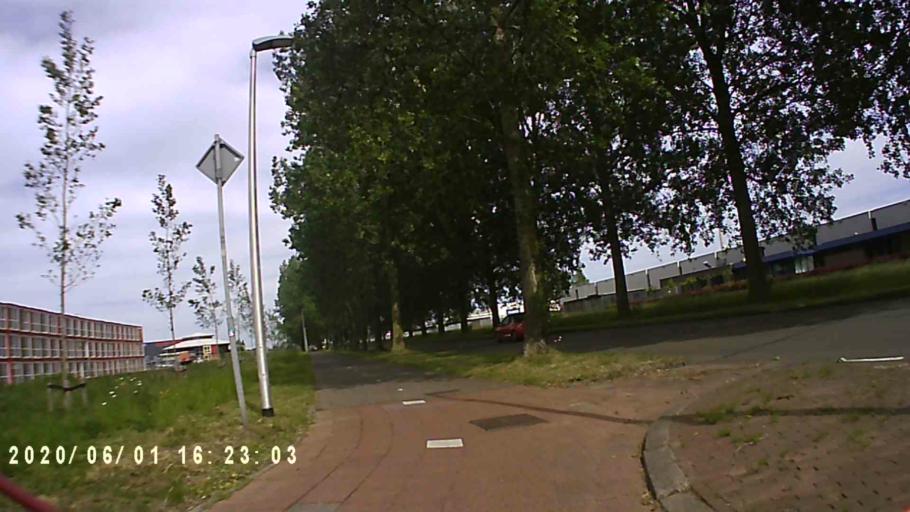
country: NL
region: Friesland
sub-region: Gemeente Leeuwarden
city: Camminghaburen
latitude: 53.1964
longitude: 5.8522
